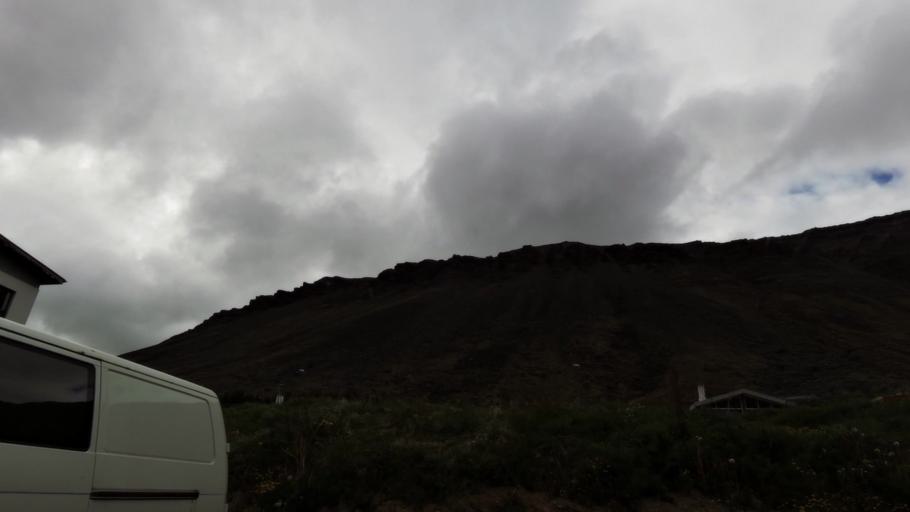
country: IS
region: Westfjords
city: Isafjoerdur
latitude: 66.0798
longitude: -23.1256
